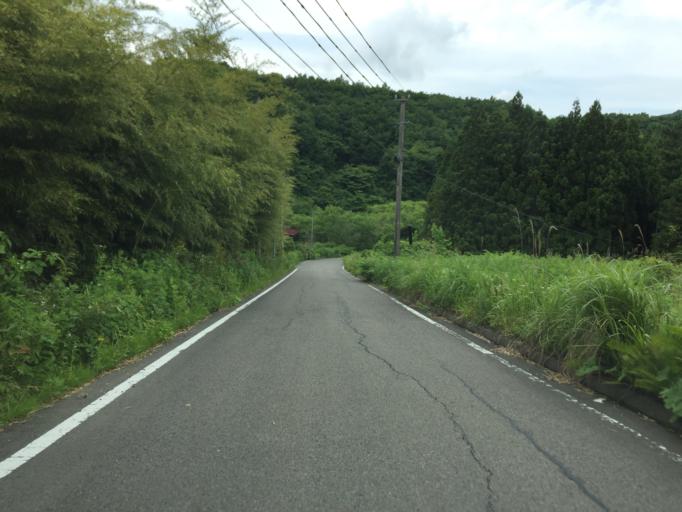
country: JP
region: Fukushima
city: Funehikimachi-funehiki
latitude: 37.4228
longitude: 140.7354
